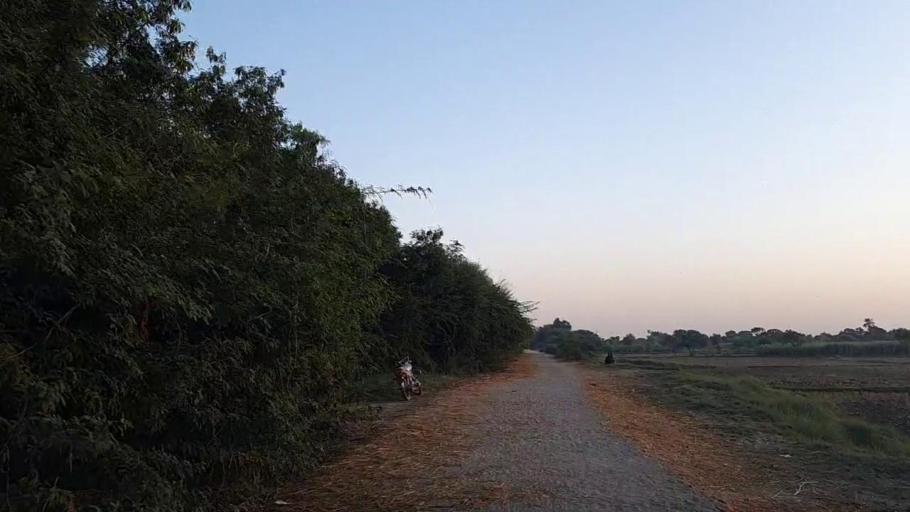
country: PK
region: Sindh
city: Mirpur Batoro
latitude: 24.6381
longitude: 68.1903
